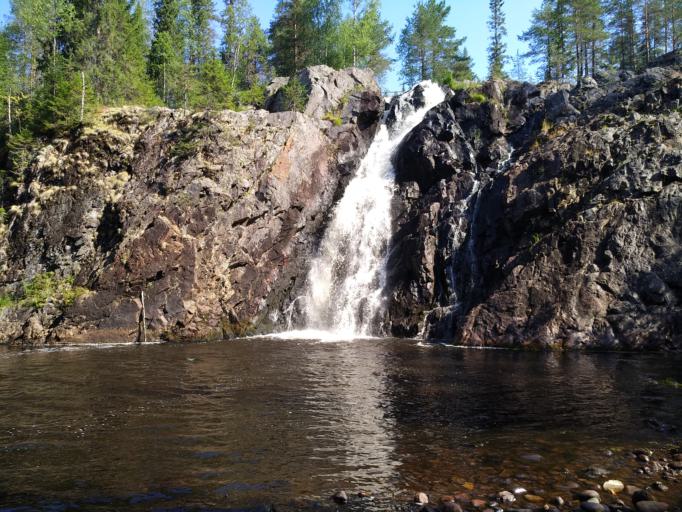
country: FI
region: Kainuu
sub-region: Kehys-Kainuu
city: Puolanka
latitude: 64.8197
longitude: 27.8762
